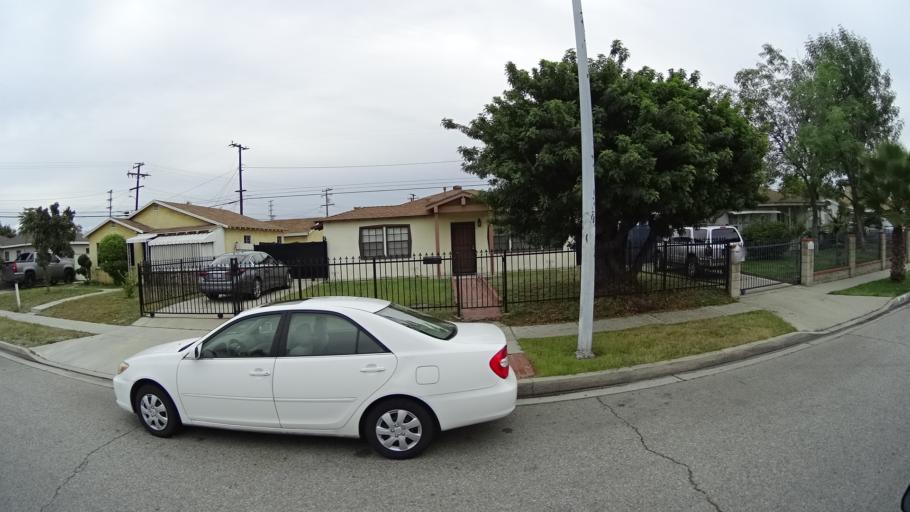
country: US
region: California
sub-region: Los Angeles County
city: Baldwin Park
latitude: 34.0779
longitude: -117.9887
